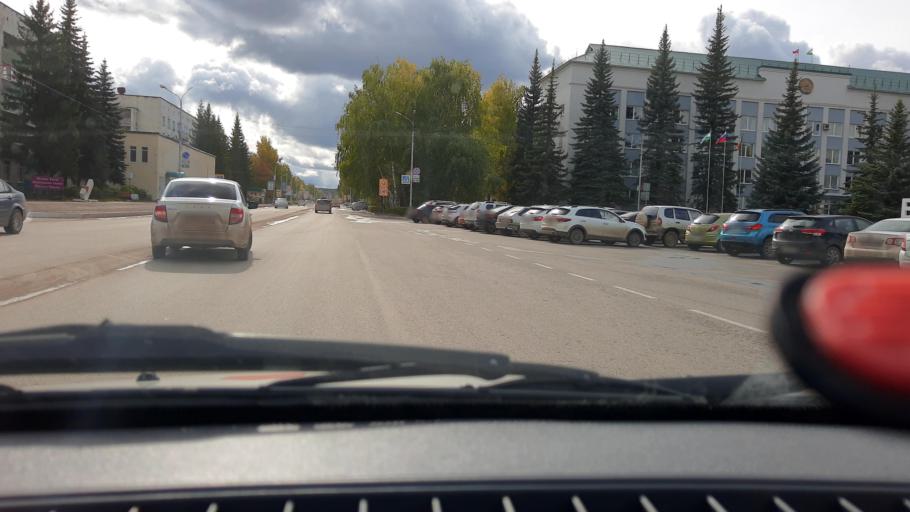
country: RU
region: Bashkortostan
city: Belebey
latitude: 54.1029
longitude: 54.1103
